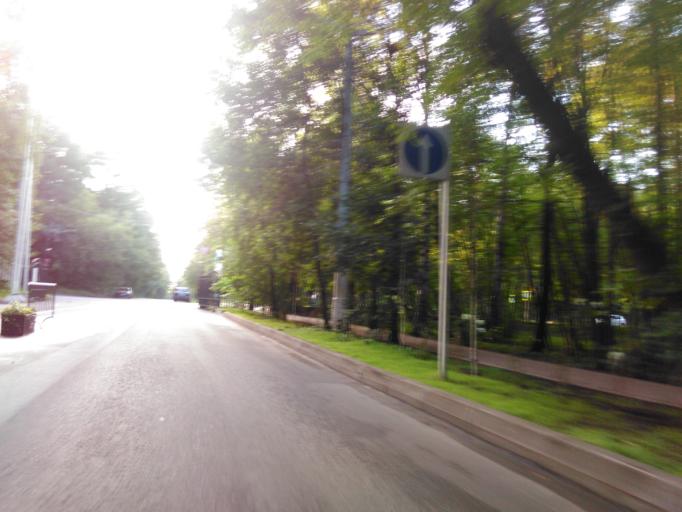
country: RU
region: Moscow
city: Sokol'niki
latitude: 55.8044
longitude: 37.6637
